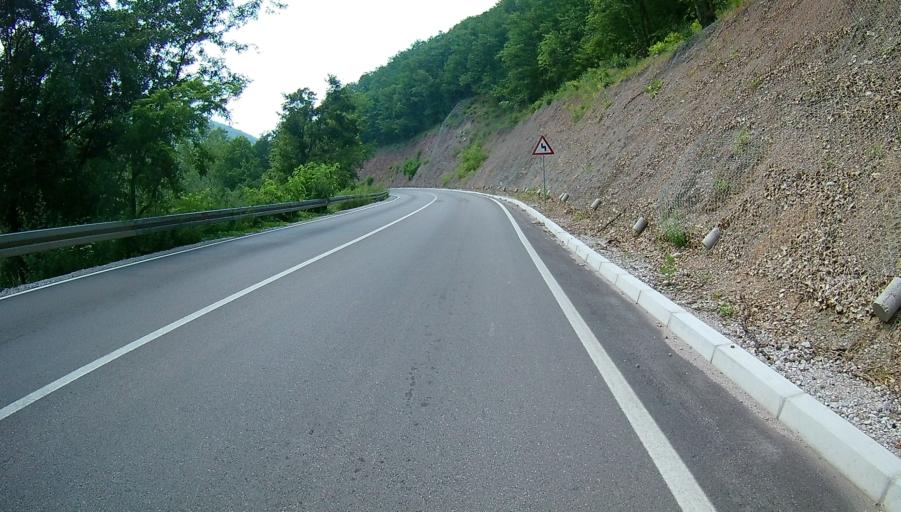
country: RS
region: Central Serbia
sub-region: Nisavski Okrug
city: Gadzin Han
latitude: 43.1677
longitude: 22.0821
